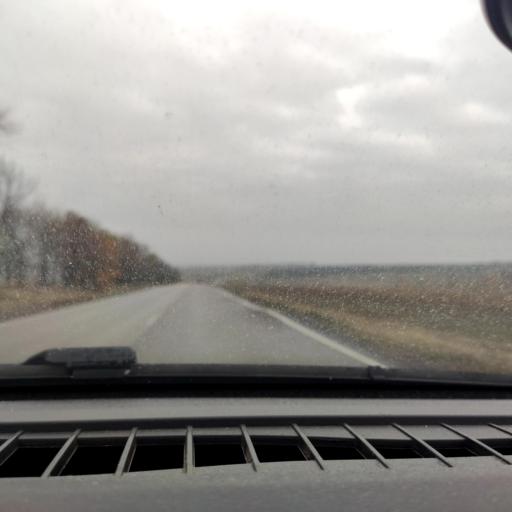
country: RU
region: Belgorod
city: Ilovka
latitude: 50.7636
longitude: 38.7439
